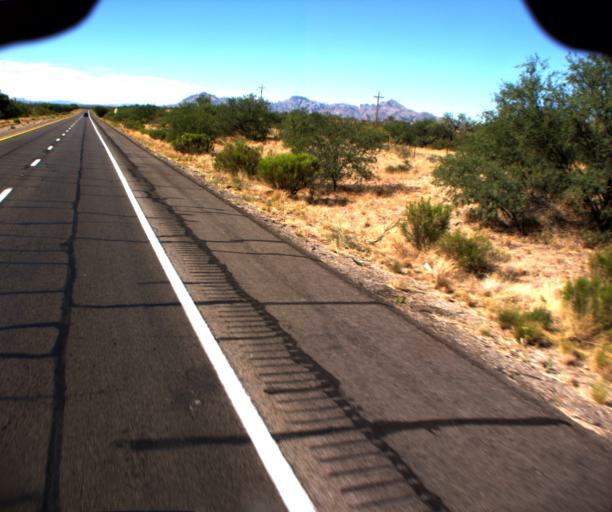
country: US
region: Arizona
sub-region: Pima County
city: Arivaca Junction
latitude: 31.6982
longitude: -111.0655
